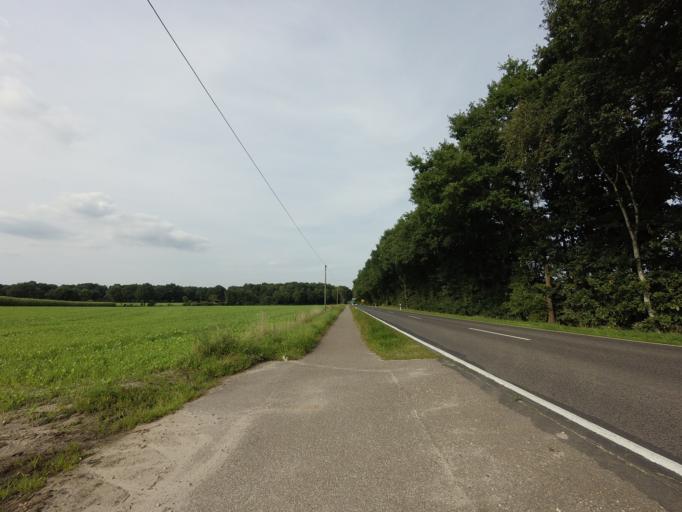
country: DE
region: Lower Saxony
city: Getelo
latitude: 52.4639
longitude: 6.8387
